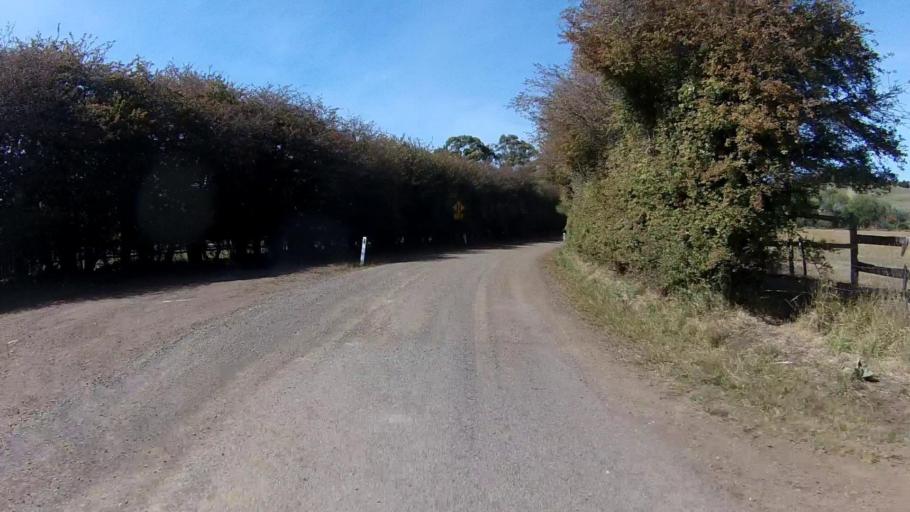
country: AU
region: Tasmania
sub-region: Sorell
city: Sorell
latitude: -42.7510
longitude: 147.6256
